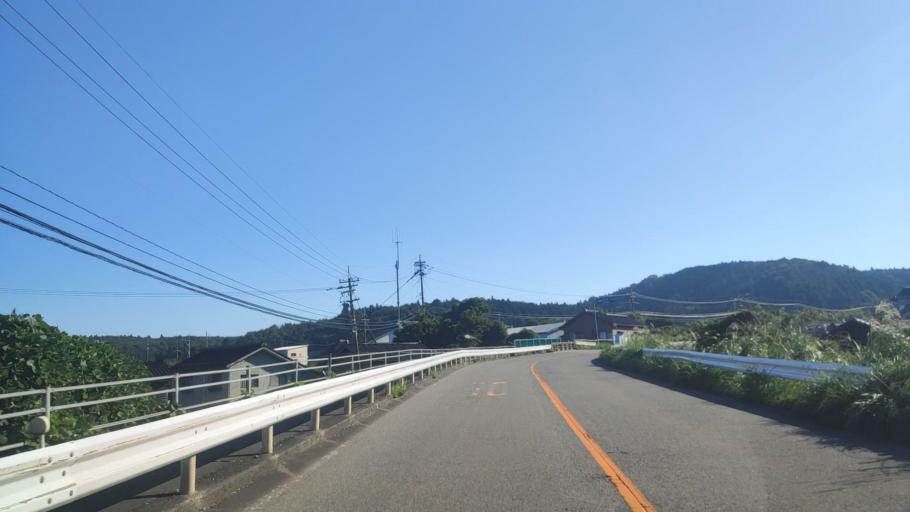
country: JP
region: Ishikawa
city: Nanao
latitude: 37.1441
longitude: 136.8721
